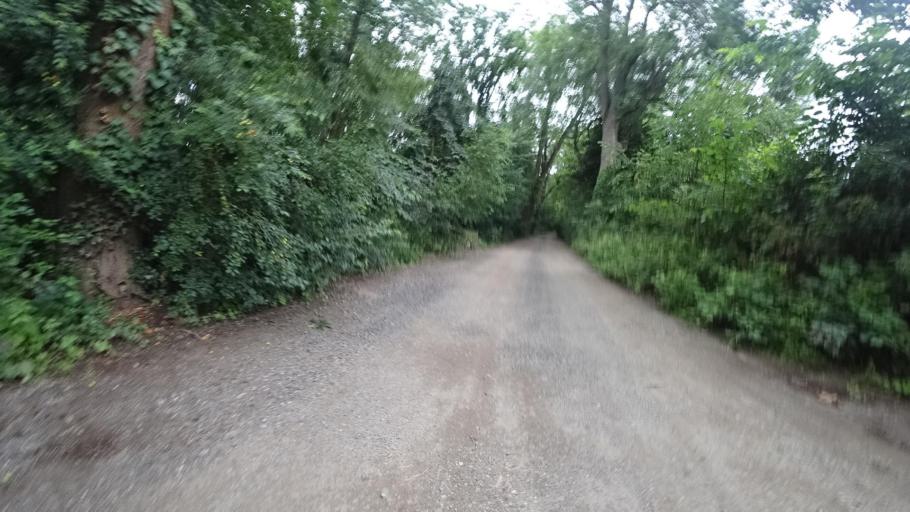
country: DE
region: Rheinland-Pfalz
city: Worms
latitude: 49.6158
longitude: 8.3664
